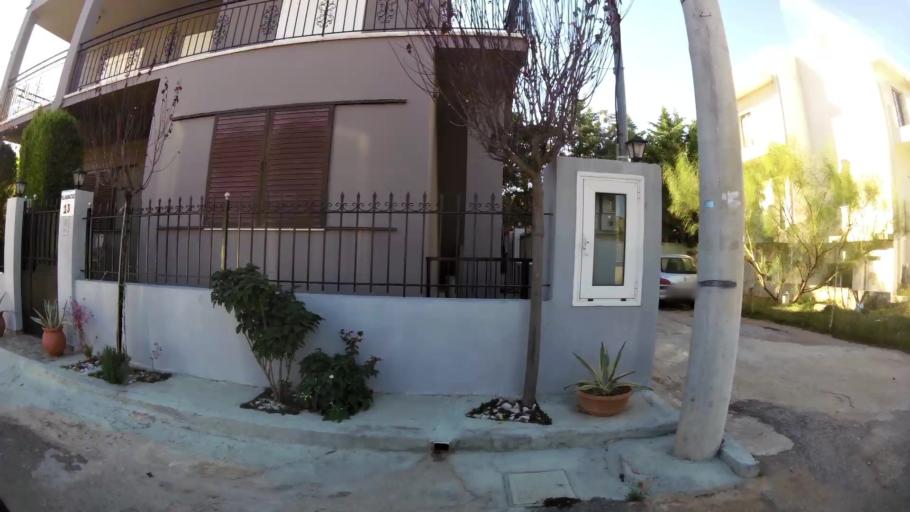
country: GR
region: Attica
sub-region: Nomarchia Anatolikis Attikis
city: Vari
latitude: 37.8327
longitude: 23.8162
